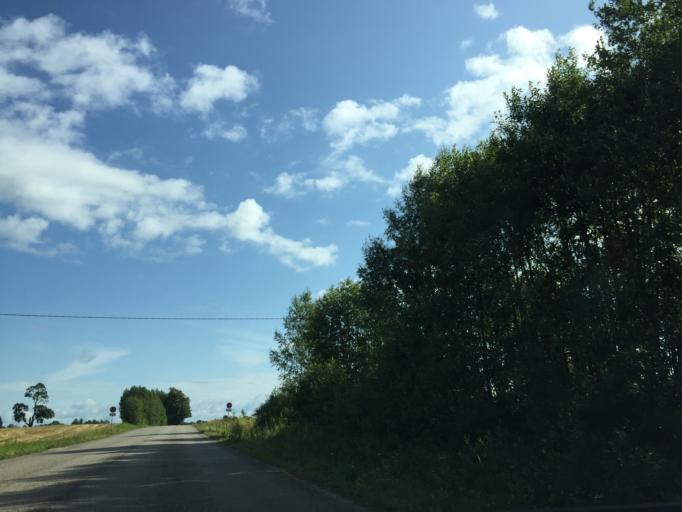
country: LV
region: Sigulda
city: Sigulda
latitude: 57.1680
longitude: 24.9118
